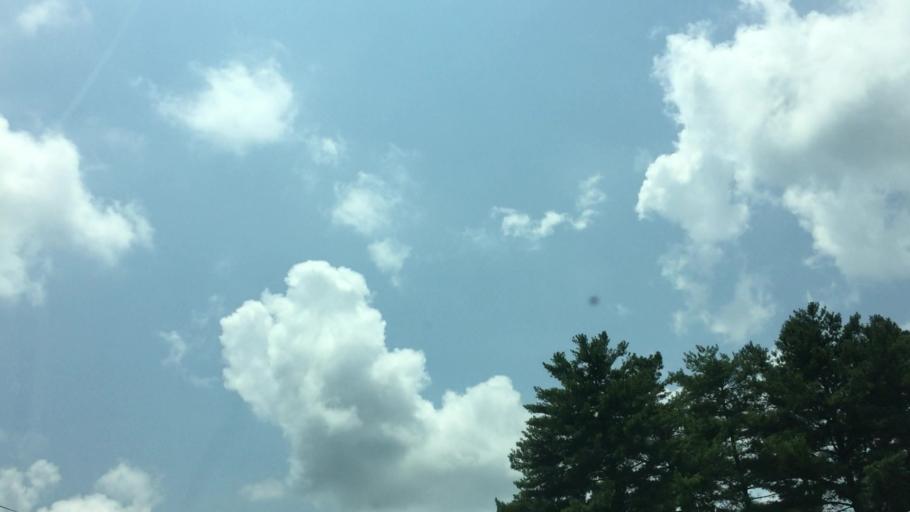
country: US
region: Georgia
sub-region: Carroll County
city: Villa Rica
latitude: 33.6105
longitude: -84.8956
